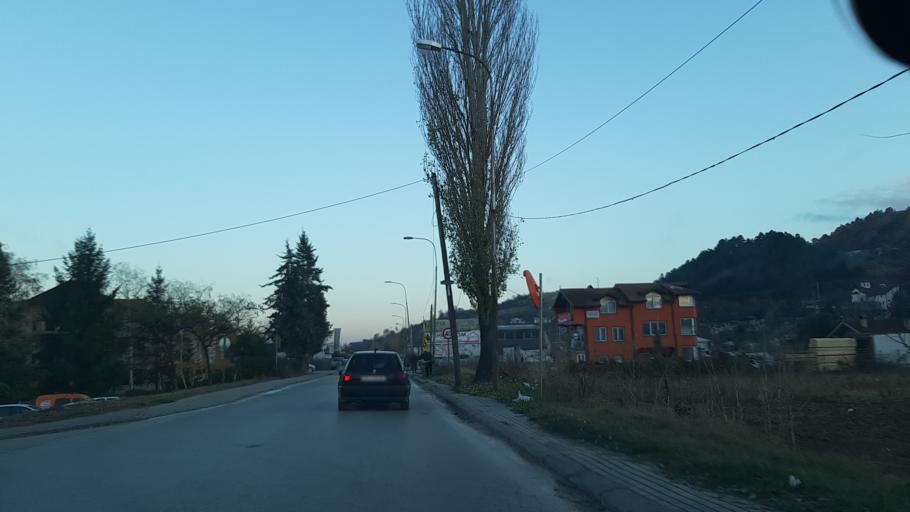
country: MK
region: Kisela Voda
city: Kisela Voda
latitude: 41.9380
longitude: 21.5092
